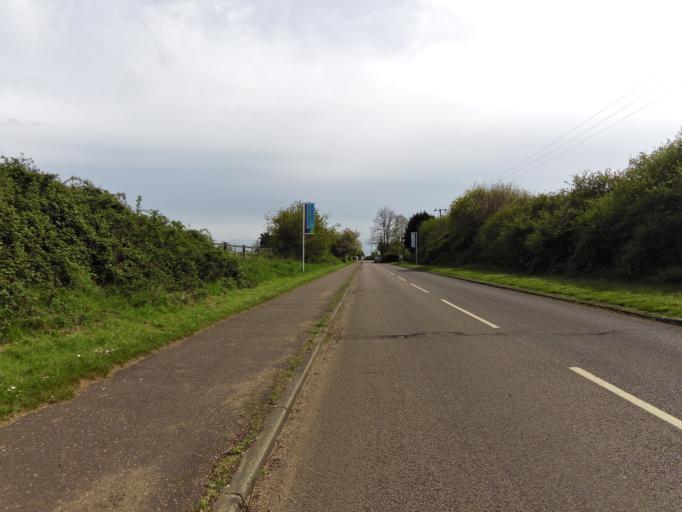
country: GB
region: England
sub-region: Essex
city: Mistley
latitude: 51.9722
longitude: 1.1375
